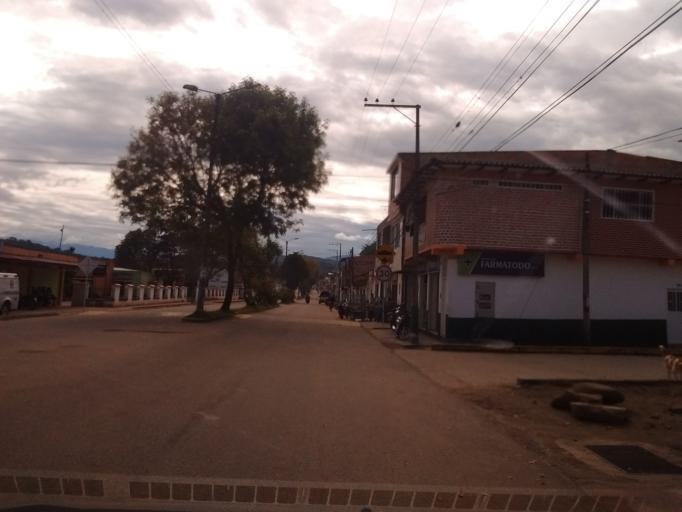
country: CO
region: Huila
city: San Agustin
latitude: 1.8774
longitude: -76.2641
